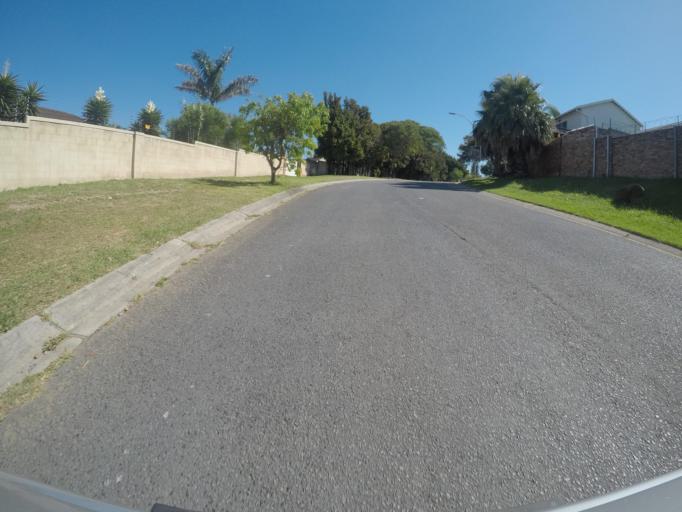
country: ZA
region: Eastern Cape
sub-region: Buffalo City Metropolitan Municipality
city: East London
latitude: -32.9567
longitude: 27.9112
